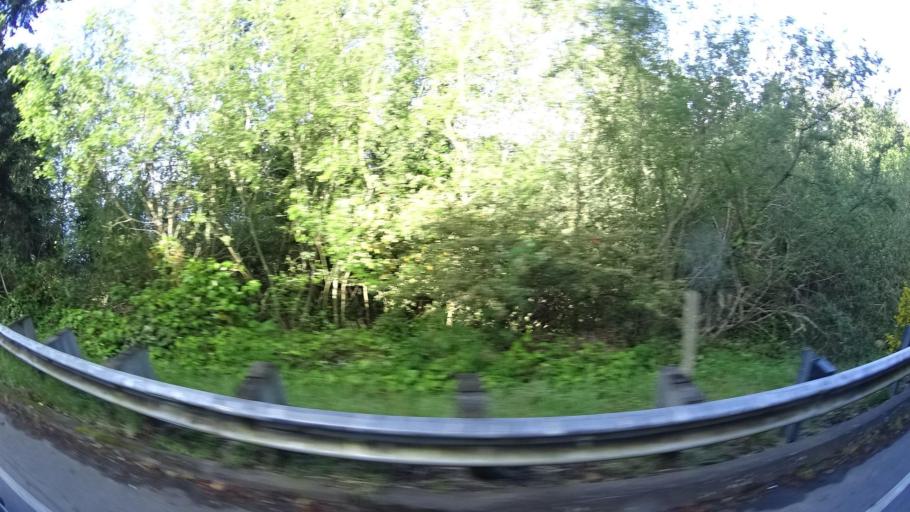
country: US
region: California
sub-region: Humboldt County
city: Westhaven-Moonstone
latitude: 41.0546
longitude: -124.1318
